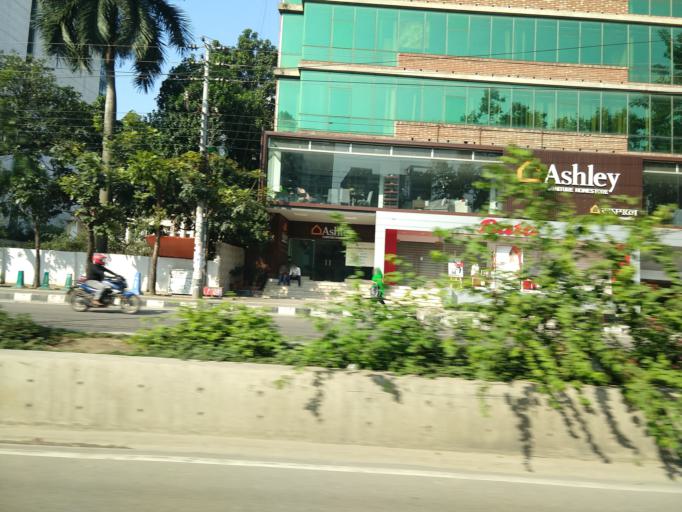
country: BD
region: Dhaka
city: Paltan
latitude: 23.7895
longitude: 90.4163
